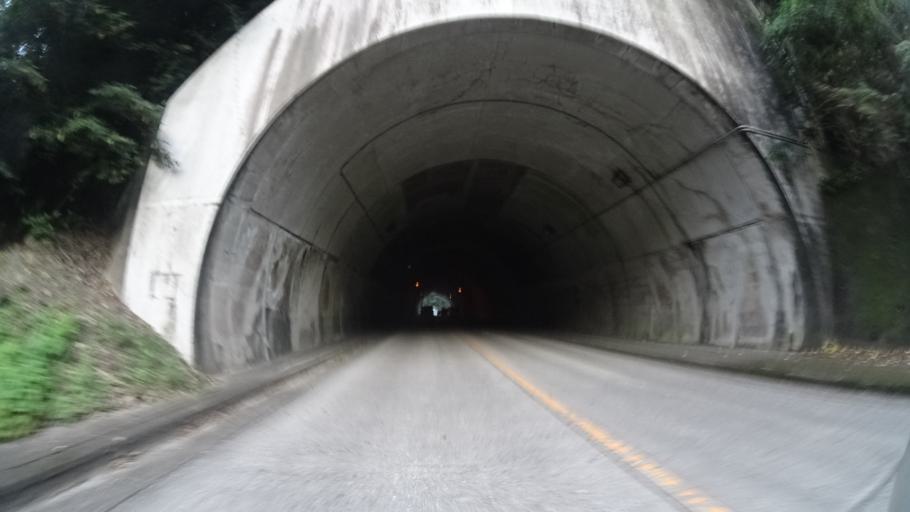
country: JP
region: Oita
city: Beppu
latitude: 33.3261
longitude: 131.4751
